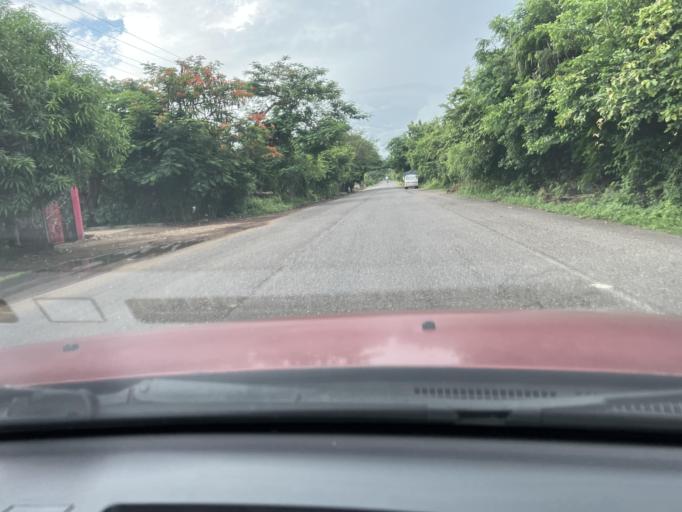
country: SV
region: La Union
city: San Alejo
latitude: 13.4164
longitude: -87.8882
